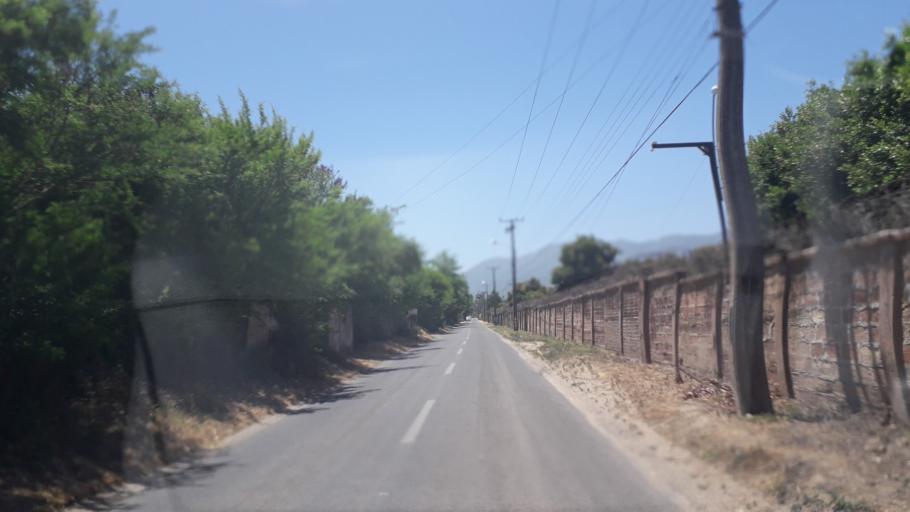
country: CL
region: Valparaiso
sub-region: Provincia de Quillota
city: Quillota
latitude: -32.9215
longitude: -71.2418
